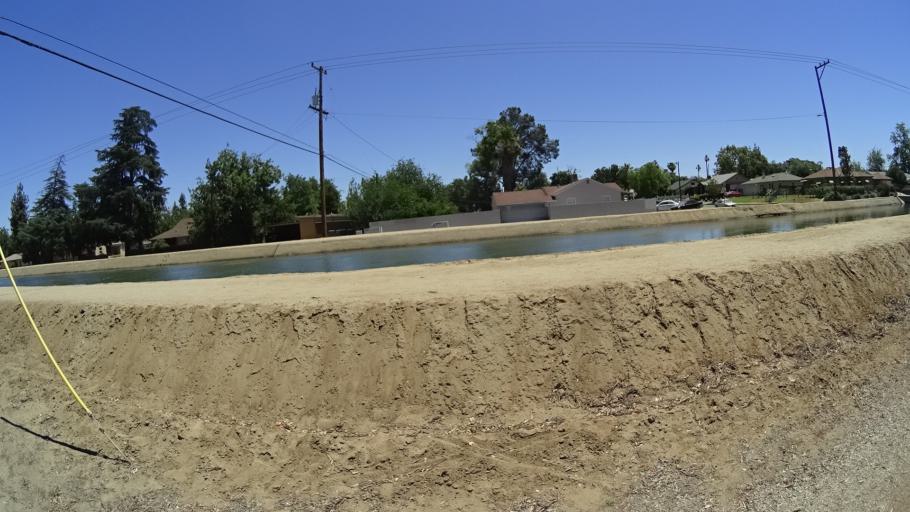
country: US
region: California
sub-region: Fresno County
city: Fresno
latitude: 36.7844
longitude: -119.7999
